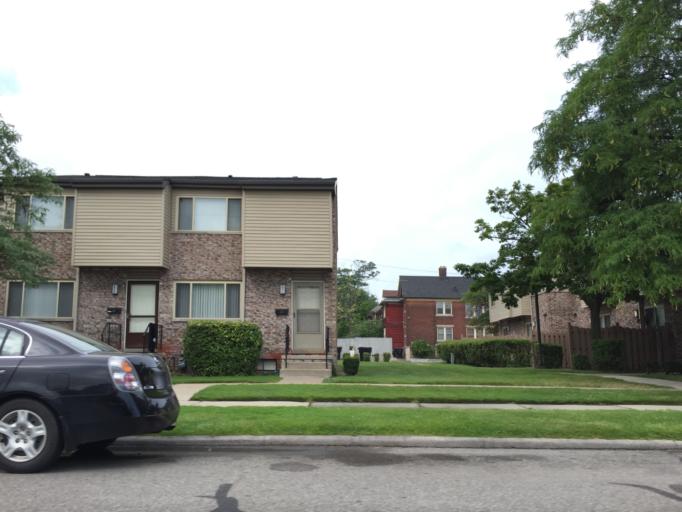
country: US
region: Michigan
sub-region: Wayne County
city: Highland Park
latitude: 42.3746
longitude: -83.0982
